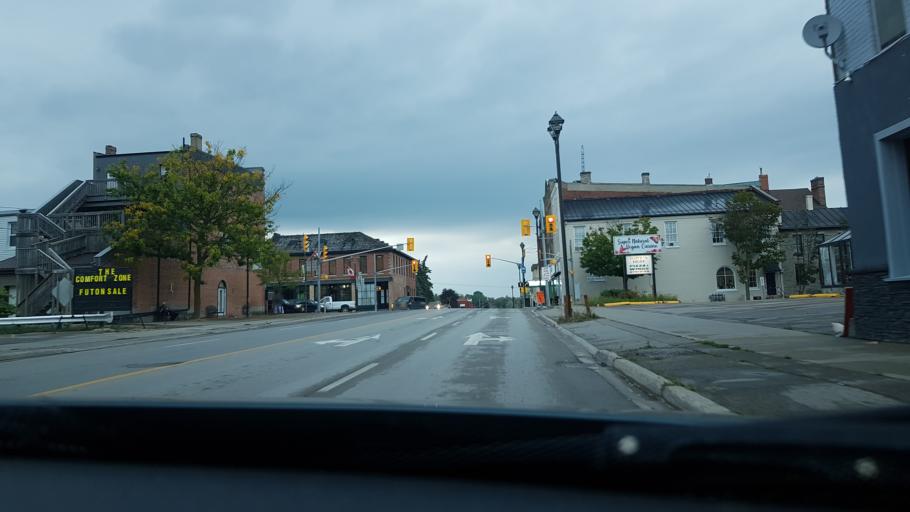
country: CA
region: Ontario
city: Omemee
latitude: 44.3549
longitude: -78.7345
